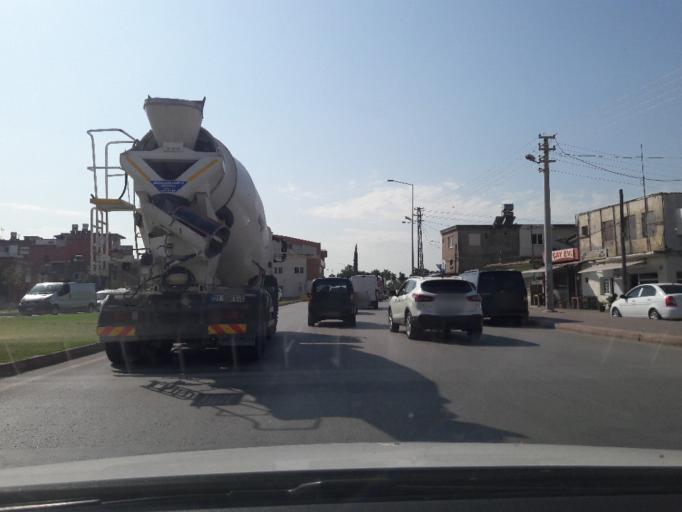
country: TR
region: Adana
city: Seyhan
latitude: 36.9949
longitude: 35.3003
